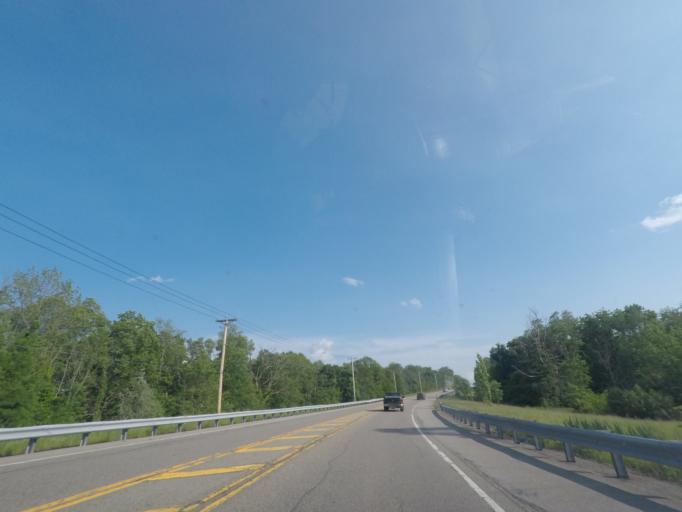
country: US
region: New York
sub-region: Orange County
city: Beaverdam Lake-Salisbury Mills
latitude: 41.4941
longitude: -74.1320
